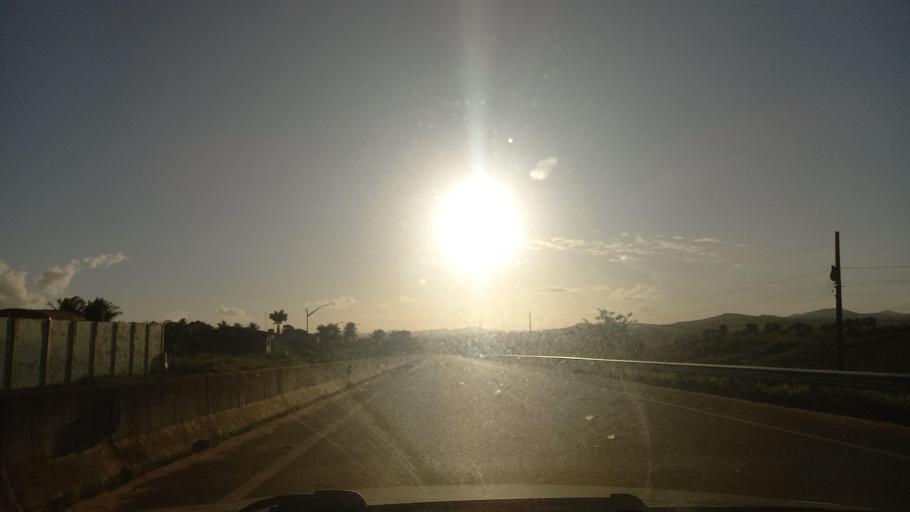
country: BR
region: Alagoas
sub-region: Limoeiro De Anadia
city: Limoeiro de Anadia
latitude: -9.7417
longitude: -36.4756
